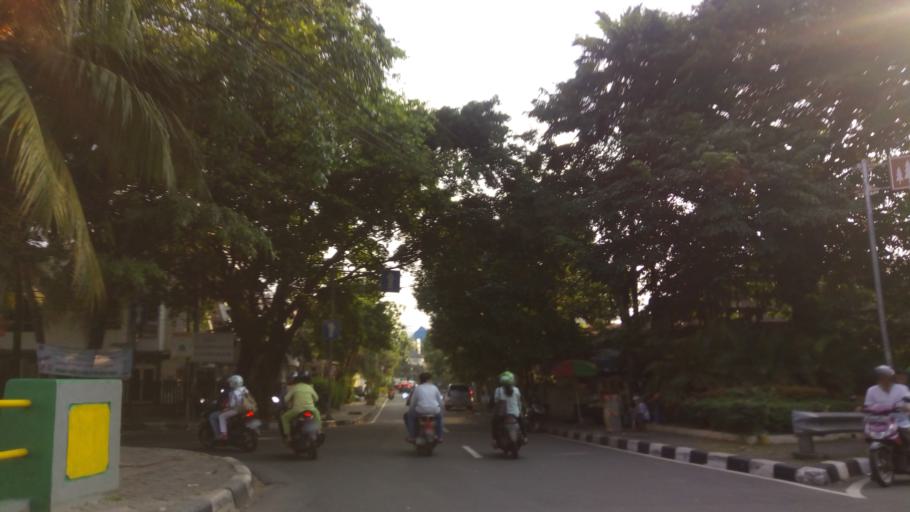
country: ID
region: Jakarta Raya
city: Jakarta
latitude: -6.1973
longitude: 106.8392
